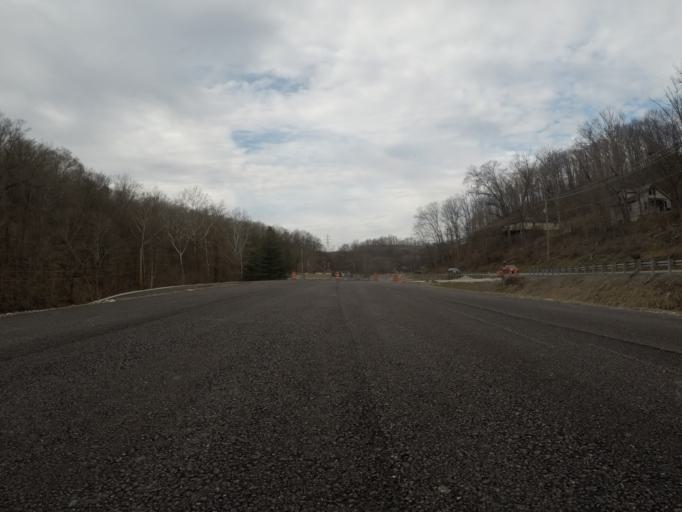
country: US
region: West Virginia
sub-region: Cabell County
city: Huntington
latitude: 38.3868
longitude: -82.3848
